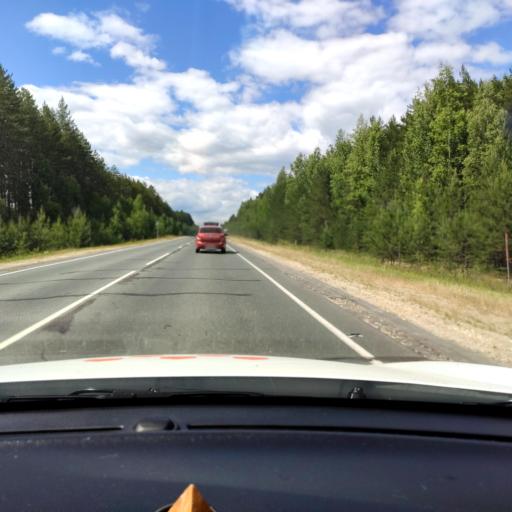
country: RU
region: Mariy-El
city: Volzhsk
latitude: 55.9011
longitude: 48.3850
